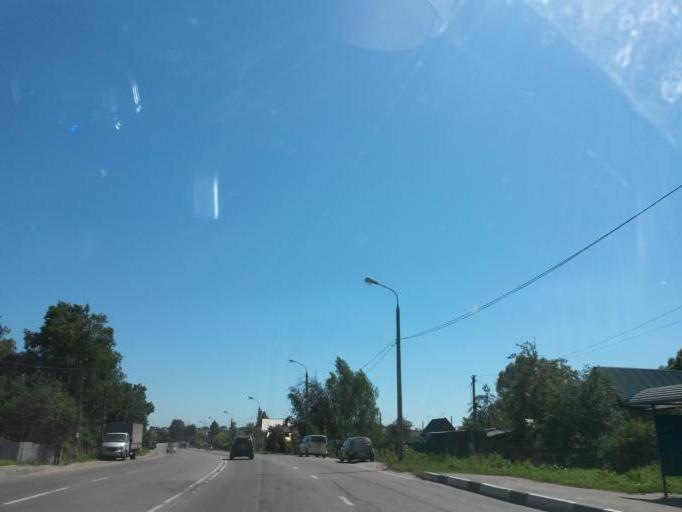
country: RU
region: Moskovskaya
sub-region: Chekhovskiy Rayon
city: Chekhov
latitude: 55.1378
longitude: 37.4511
